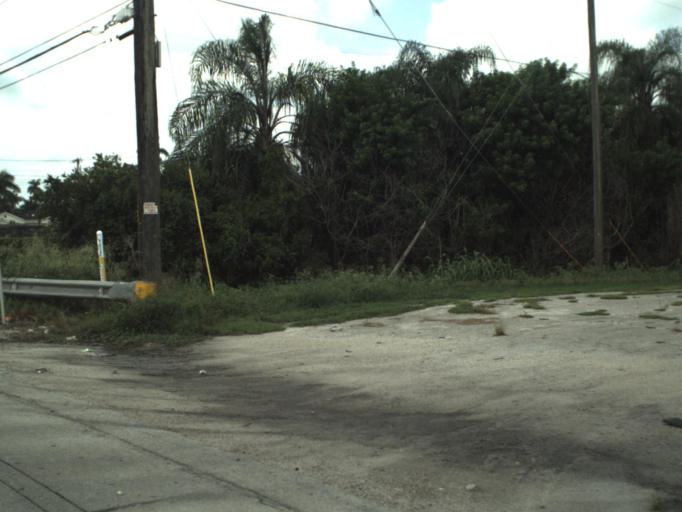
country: US
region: Florida
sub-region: Palm Beach County
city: Belle Glade
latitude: 26.6971
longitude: -80.6840
